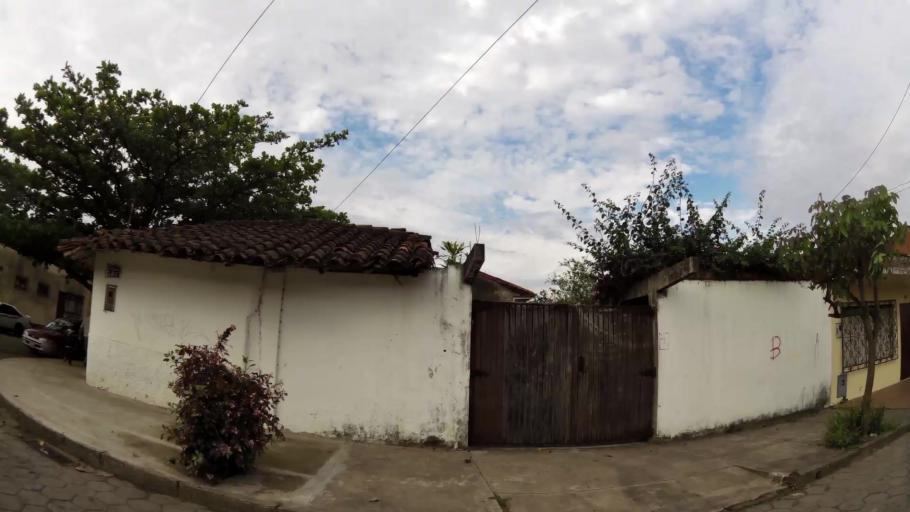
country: BO
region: Santa Cruz
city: Santa Cruz de la Sierra
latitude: -17.7874
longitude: -63.1745
